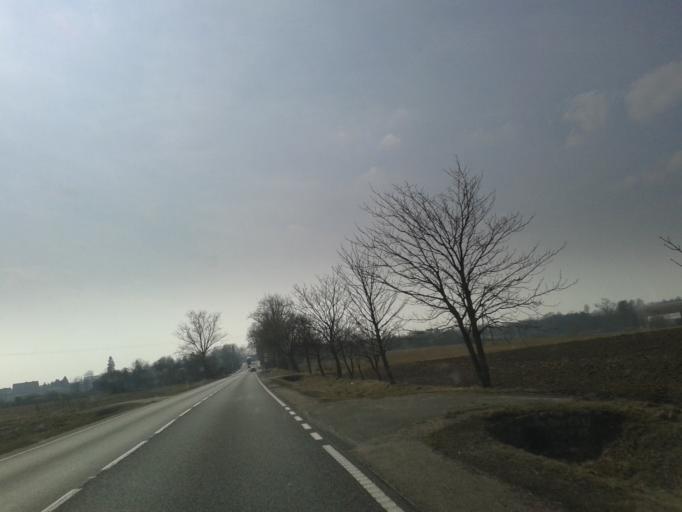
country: PL
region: Pomeranian Voivodeship
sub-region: Powiat czluchowski
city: Debrzno
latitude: 53.6026
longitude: 17.1420
